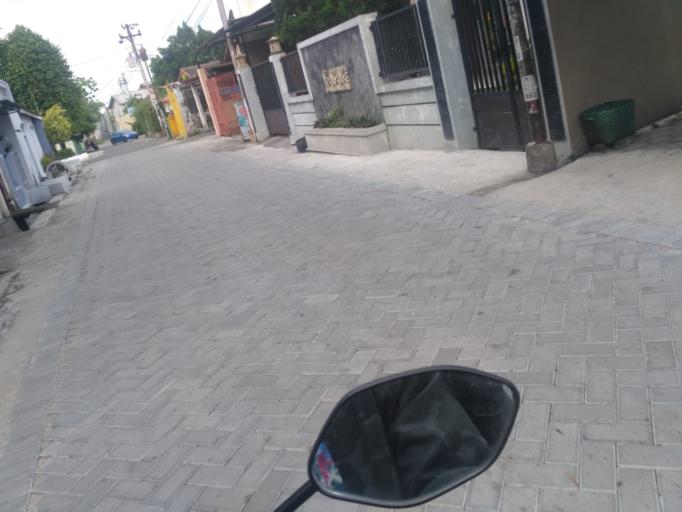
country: ID
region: Daerah Istimewa Yogyakarta
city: Melati
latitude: -7.7550
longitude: 110.3645
